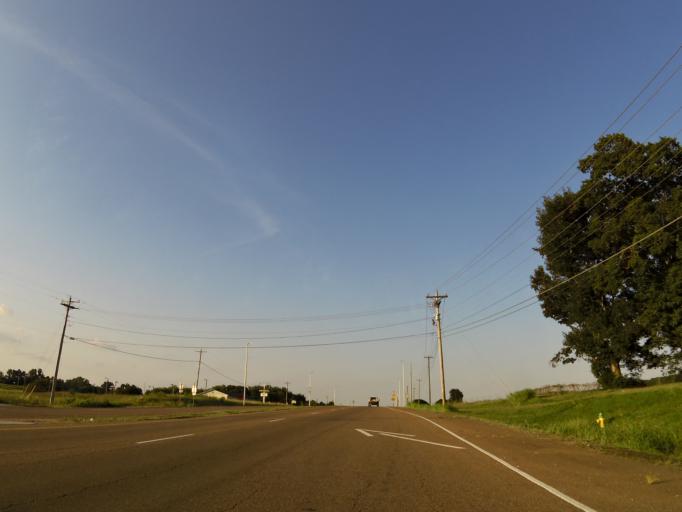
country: US
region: Tennessee
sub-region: McMinn County
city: Athens
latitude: 35.4807
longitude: -84.5920
